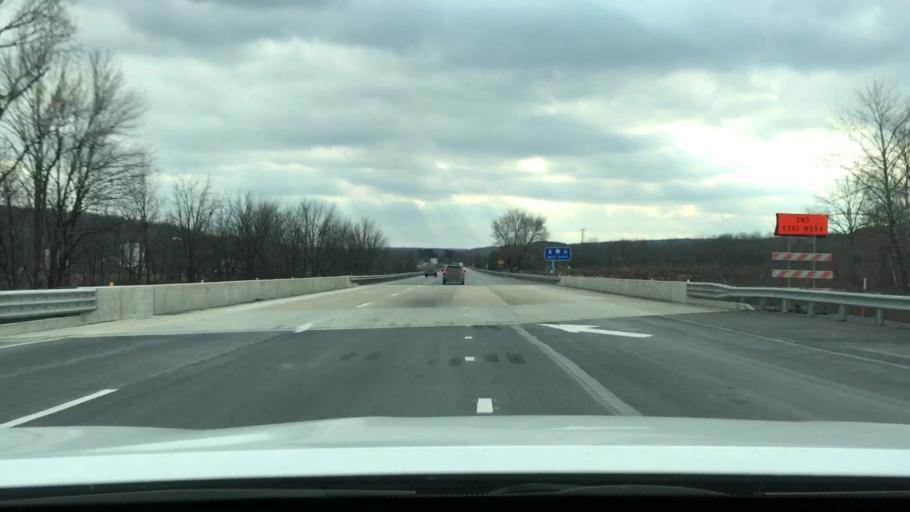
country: US
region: Pennsylvania
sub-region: Monroe County
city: Saylorsburg
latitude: 40.9562
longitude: -75.2871
